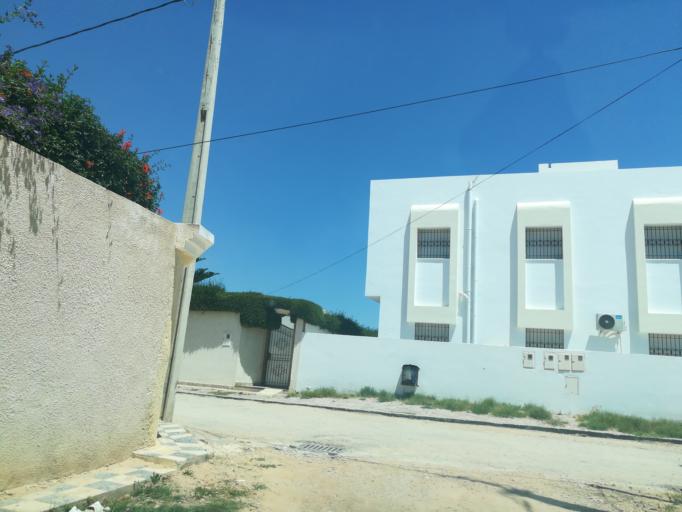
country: TN
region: Safaqis
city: Al Qarmadah
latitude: 34.8141
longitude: 10.7601
